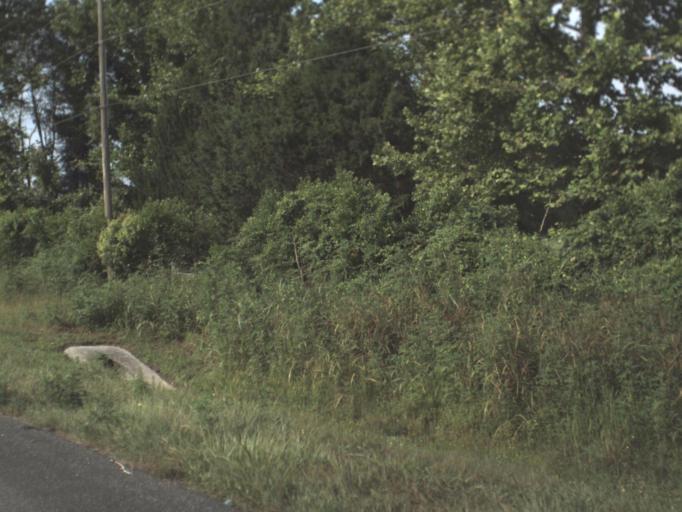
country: US
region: Florida
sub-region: Taylor County
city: Perry
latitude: 30.1855
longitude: -83.6018
